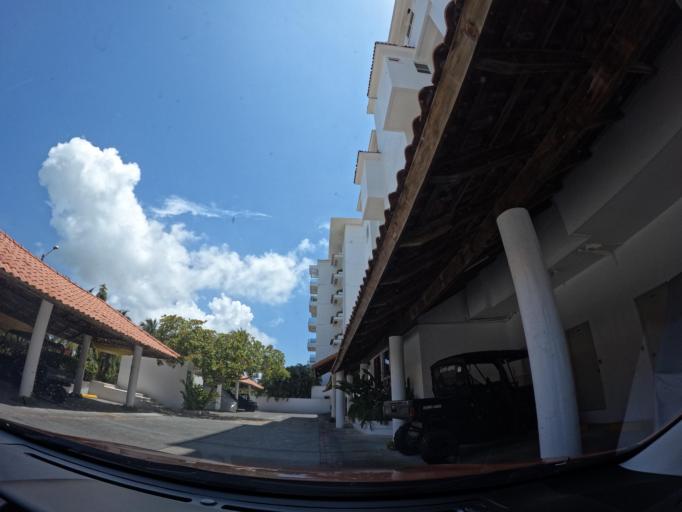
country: GT
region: Escuintla
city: Puerto San Jose
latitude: 13.9297
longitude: -90.9405
